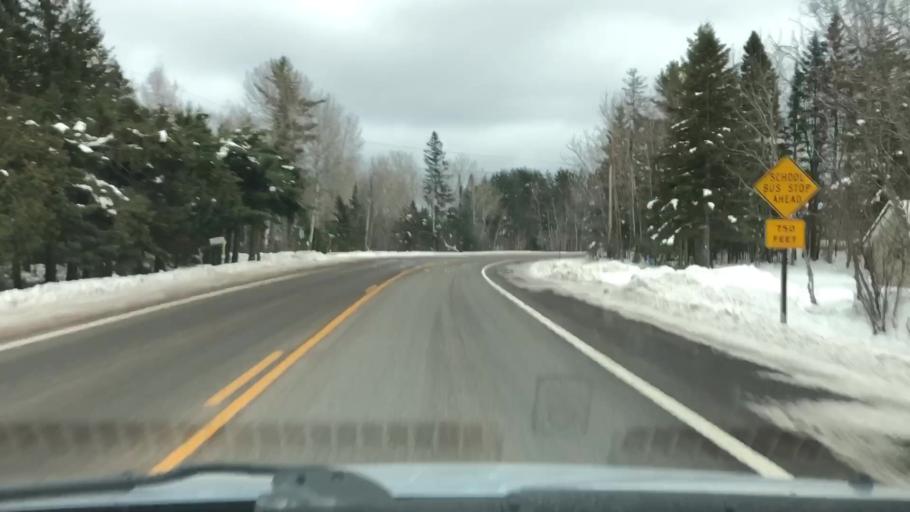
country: US
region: Minnesota
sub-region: Carlton County
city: Esko
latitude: 46.6856
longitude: -92.3648
